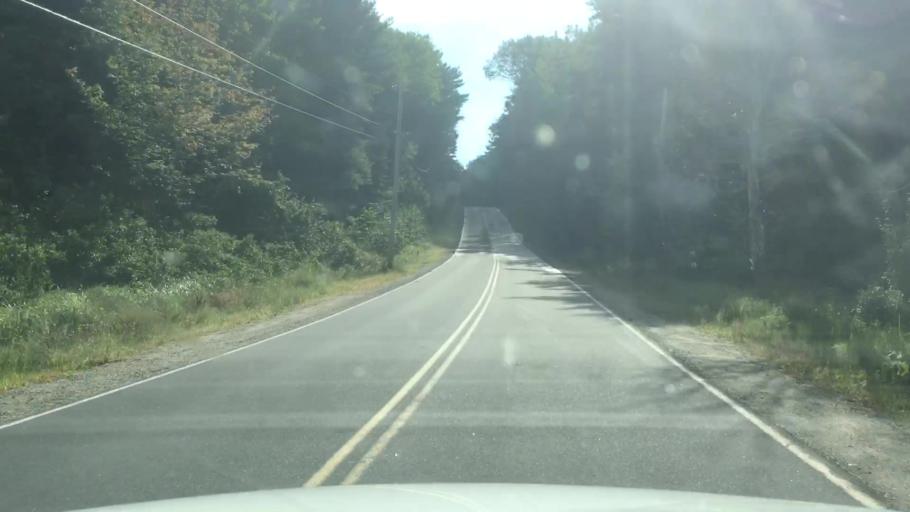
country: US
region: Maine
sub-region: Kennebec County
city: Gardiner
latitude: 44.1638
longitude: -69.8072
